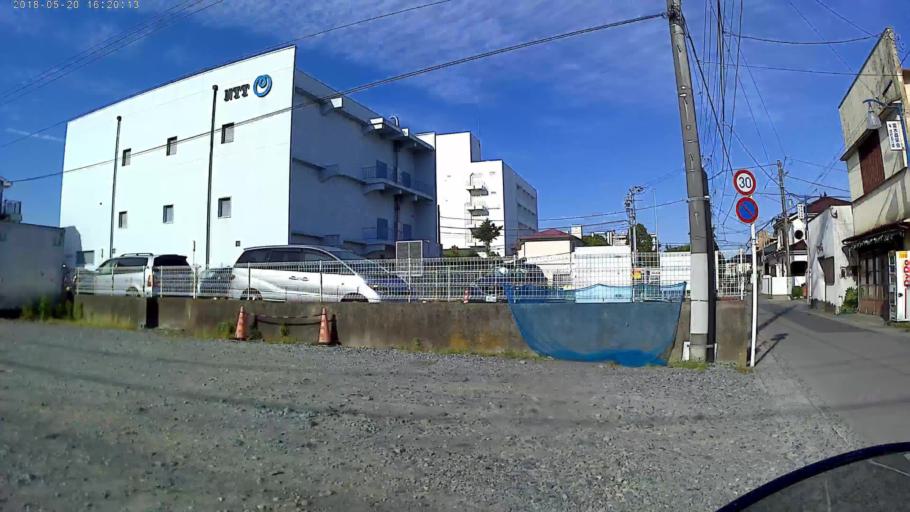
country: JP
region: Kanagawa
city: Odawara
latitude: 35.2962
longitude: 139.1479
